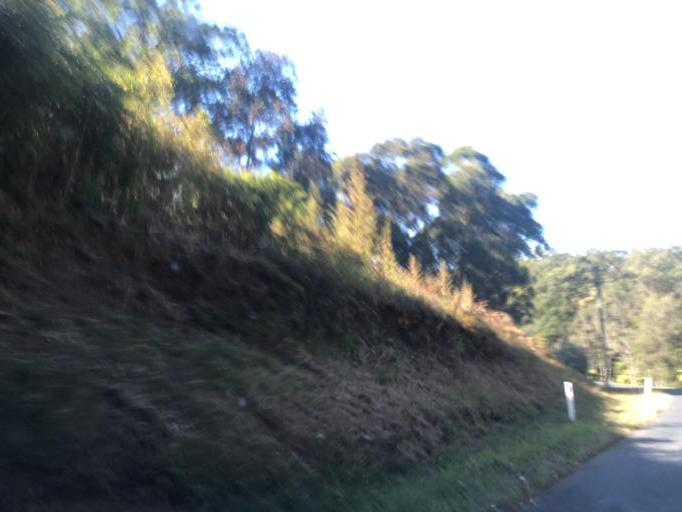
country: AU
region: New South Wales
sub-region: Coffs Harbour
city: Toormina
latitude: -30.3473
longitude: 153.0859
